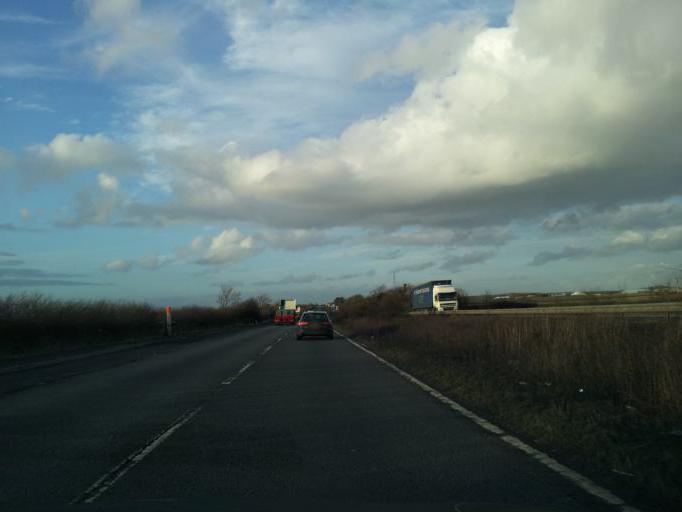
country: GB
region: England
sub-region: District of Rutland
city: Greetham
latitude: 52.7714
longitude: -0.6114
